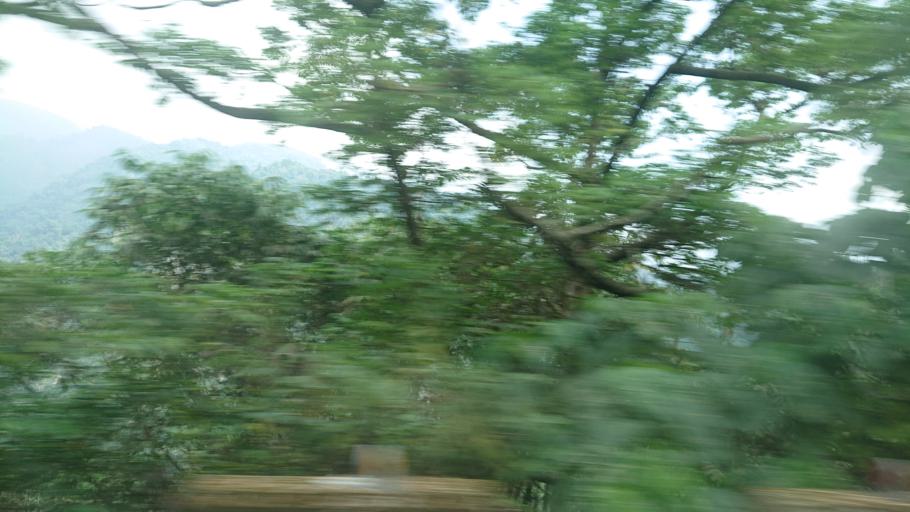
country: TW
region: Taiwan
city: Lugu
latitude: 23.5866
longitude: 120.6977
